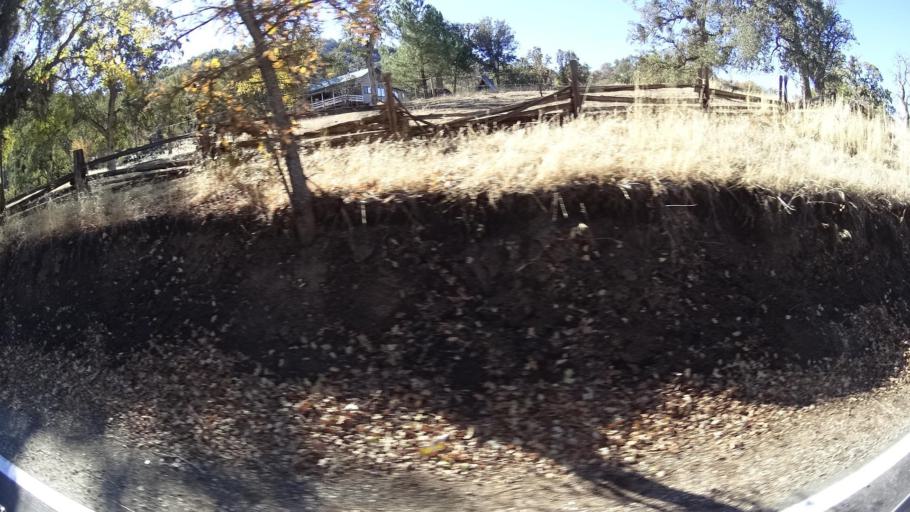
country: US
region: California
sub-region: Kern County
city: Alta Sierra
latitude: 35.7355
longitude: -118.6611
